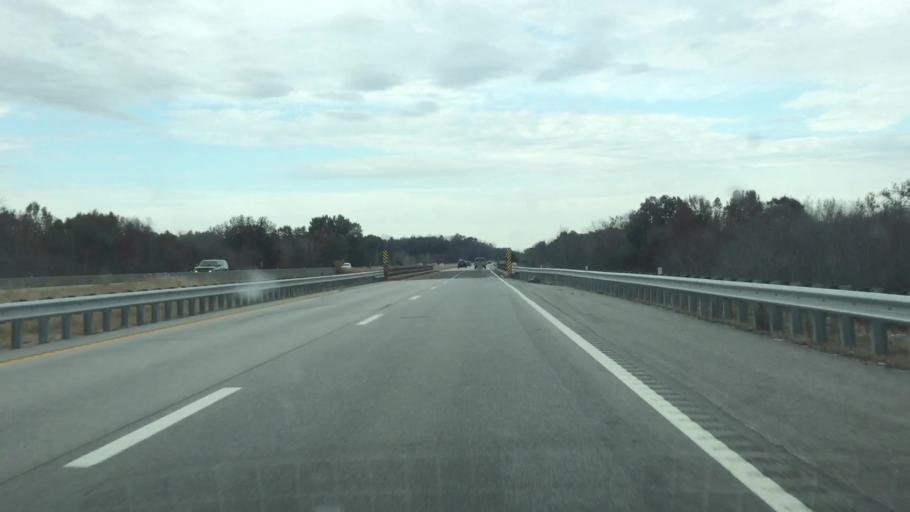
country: US
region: Missouri
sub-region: Henry County
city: Clinton
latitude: 38.2262
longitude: -93.7620
